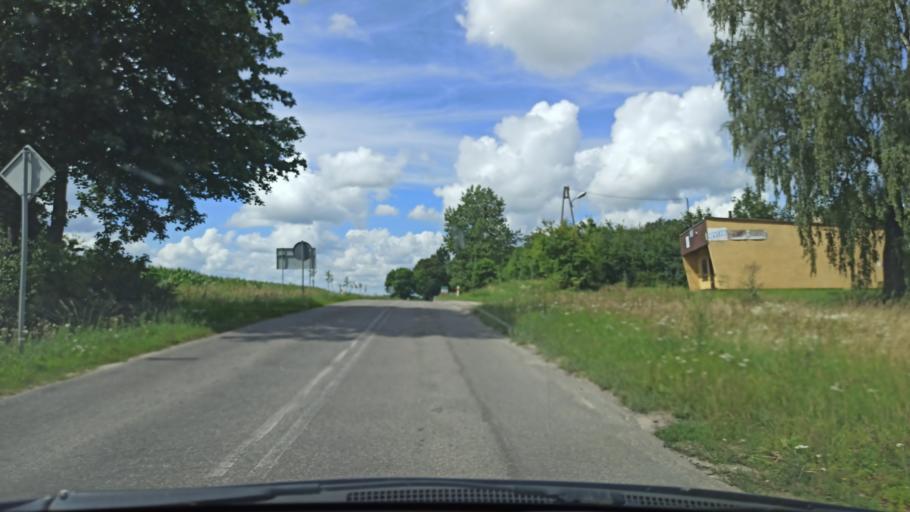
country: PL
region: Warmian-Masurian Voivodeship
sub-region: Powiat ostrodzki
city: Morag
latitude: 53.8563
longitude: 19.9808
